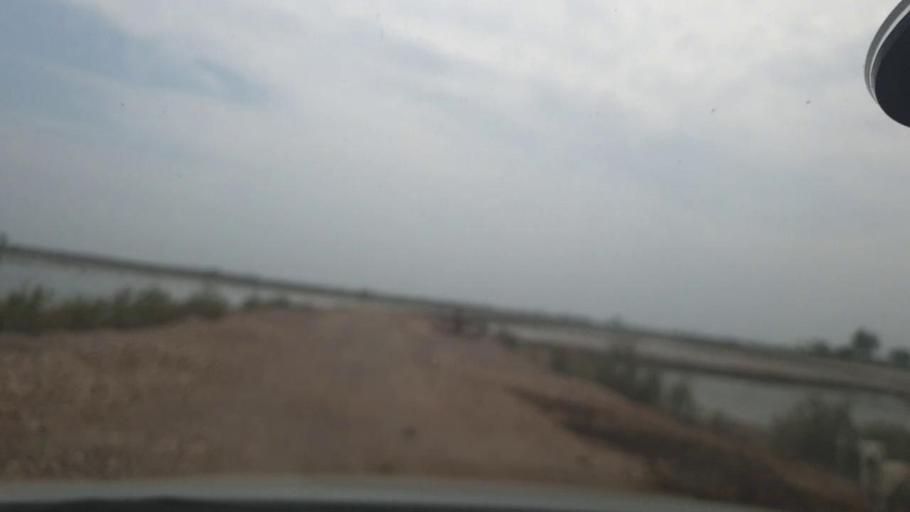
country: PK
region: Balochistan
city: Garhi Khairo
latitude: 28.0159
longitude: 68.0435
